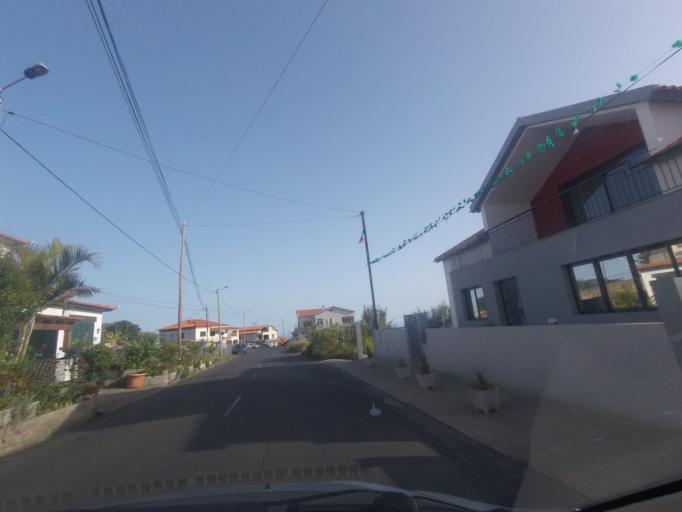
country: PT
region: Madeira
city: Ponta do Sol
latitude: 32.6987
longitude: -17.1131
